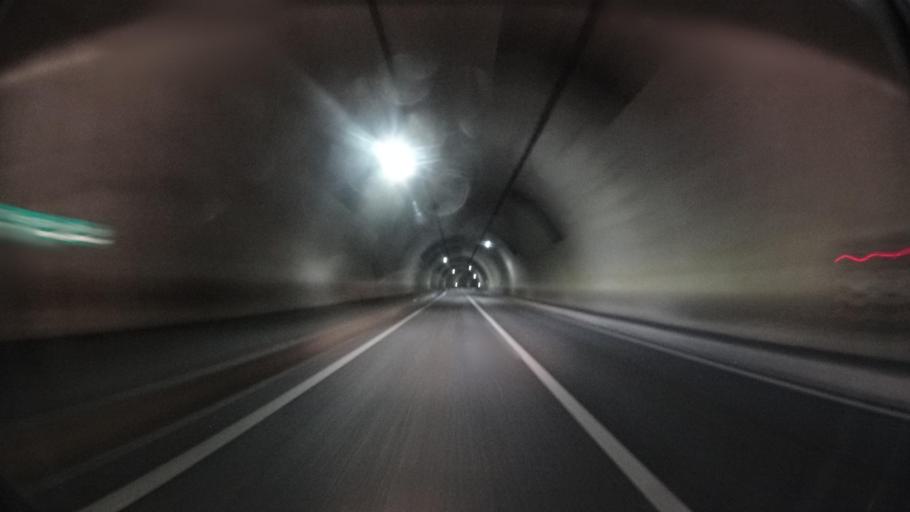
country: JP
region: Kyoto
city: Maizuru
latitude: 35.5226
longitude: 135.3492
